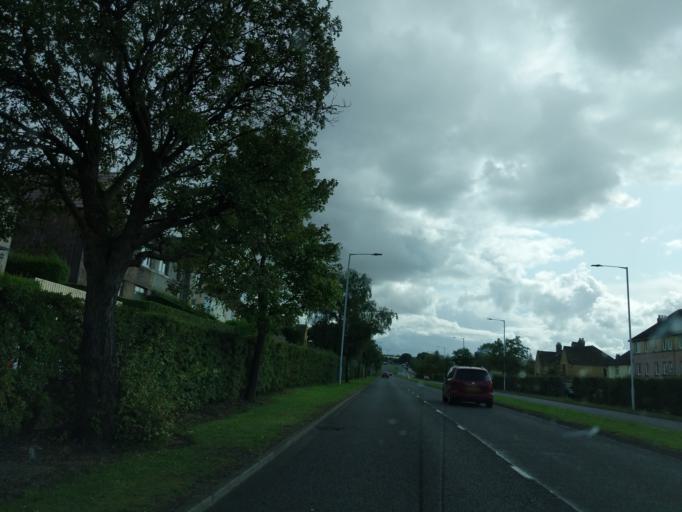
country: GB
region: Scotland
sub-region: Fife
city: Rosyth
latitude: 56.0410
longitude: -3.4276
